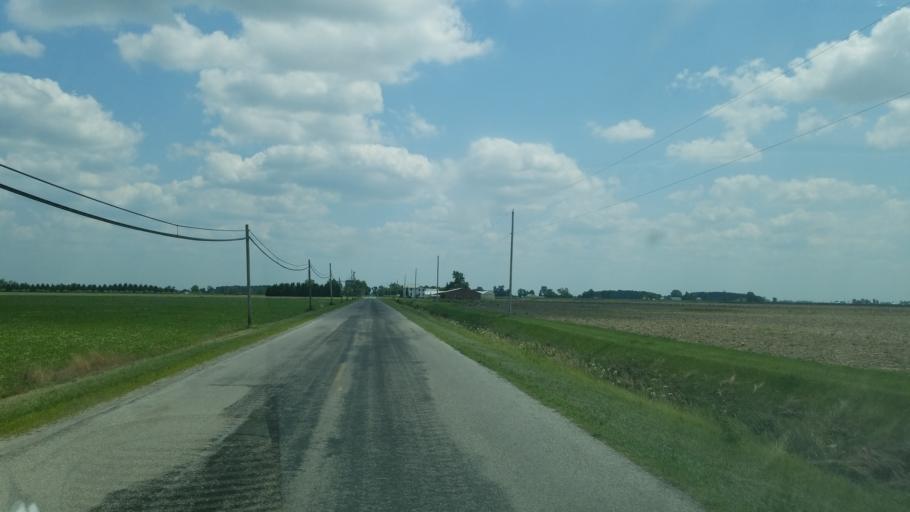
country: US
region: Ohio
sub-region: Henry County
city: Liberty Center
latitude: 41.3418
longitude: -84.0159
